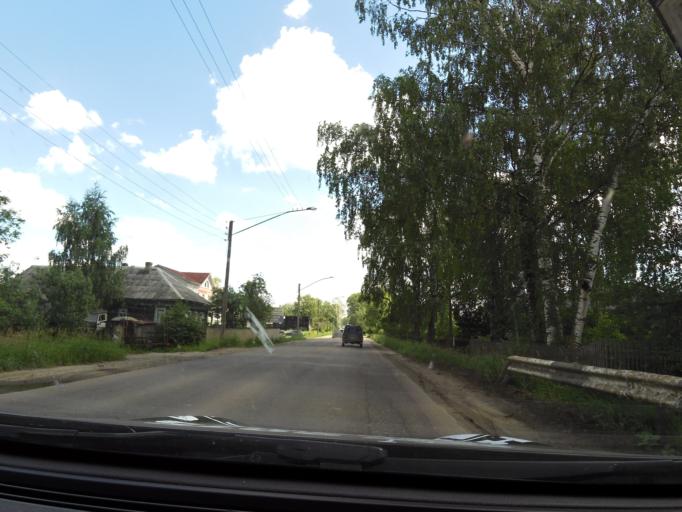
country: RU
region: Vologda
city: Vologda
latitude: 59.2389
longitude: 39.7996
